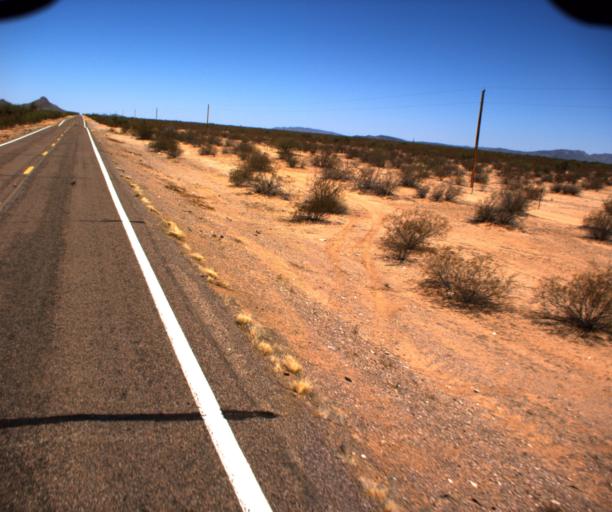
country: US
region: Arizona
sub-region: Pima County
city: Ajo
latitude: 32.1973
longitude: -112.4701
